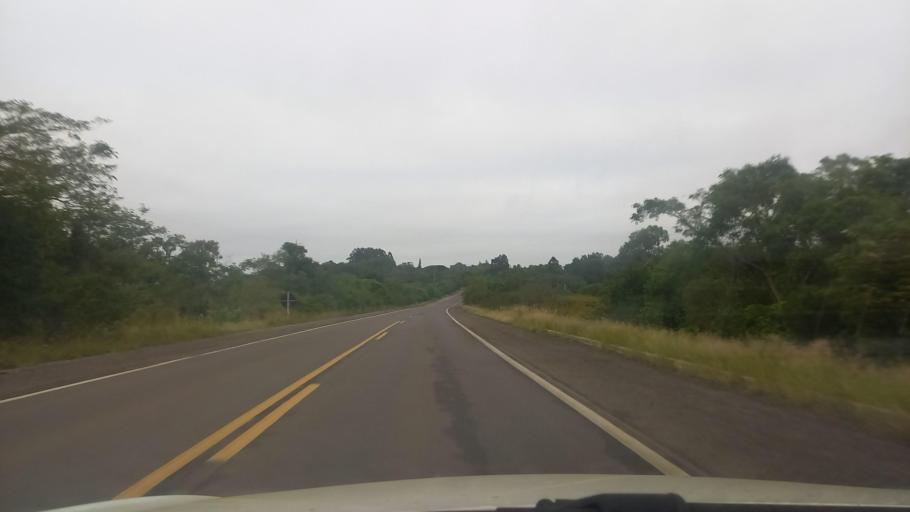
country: BR
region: Rio Grande do Sul
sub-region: Sao Pedro Do Sul
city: Sao Pedro do Sul
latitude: -29.7806
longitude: -54.1040
